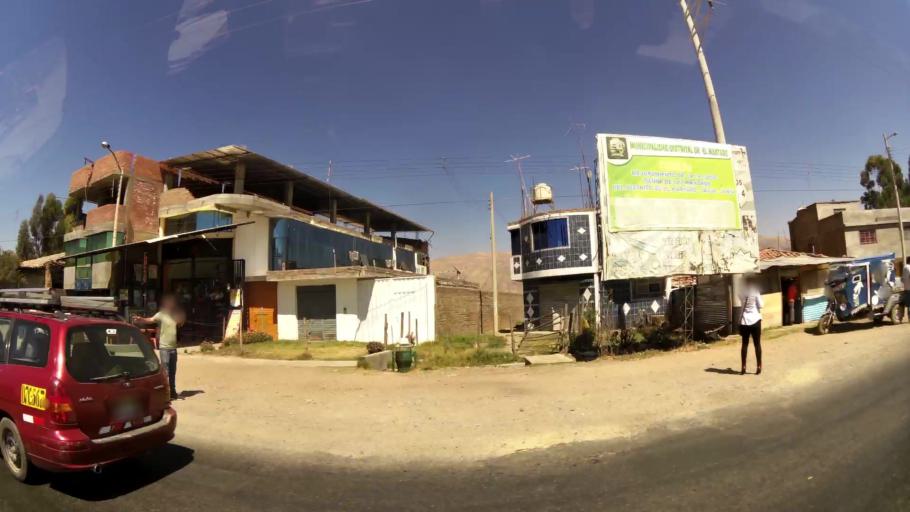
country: PE
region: Junin
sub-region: Provincia de Jauja
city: San Lorenzo
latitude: -11.8336
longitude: -75.3973
